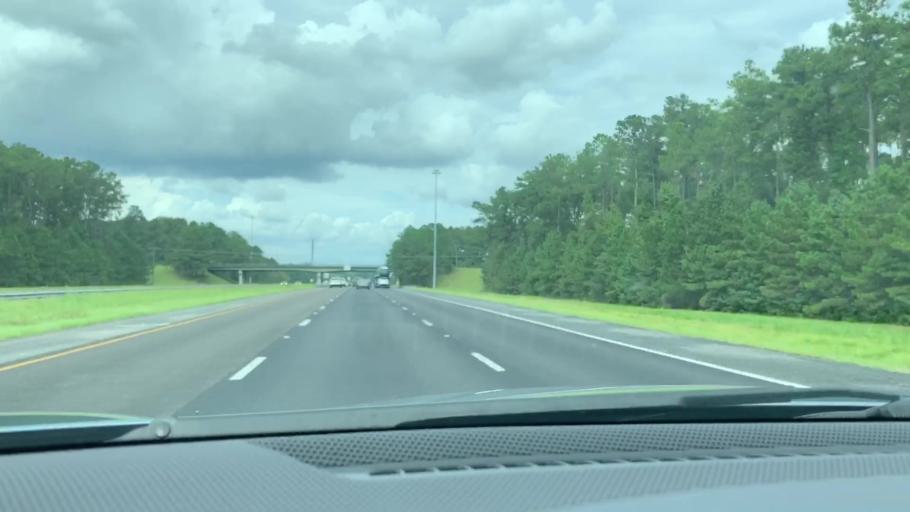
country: US
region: Georgia
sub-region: Liberty County
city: Midway
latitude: 31.7759
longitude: -81.3790
